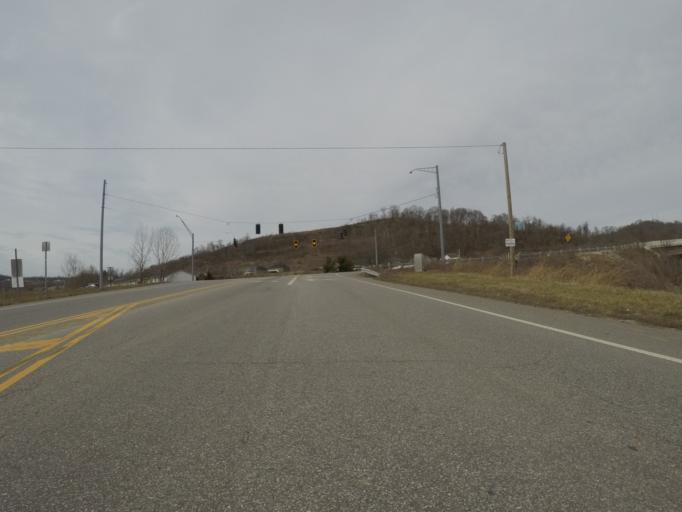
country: US
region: West Virginia
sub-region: Cabell County
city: Pea Ridge
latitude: 38.4448
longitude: -82.3806
